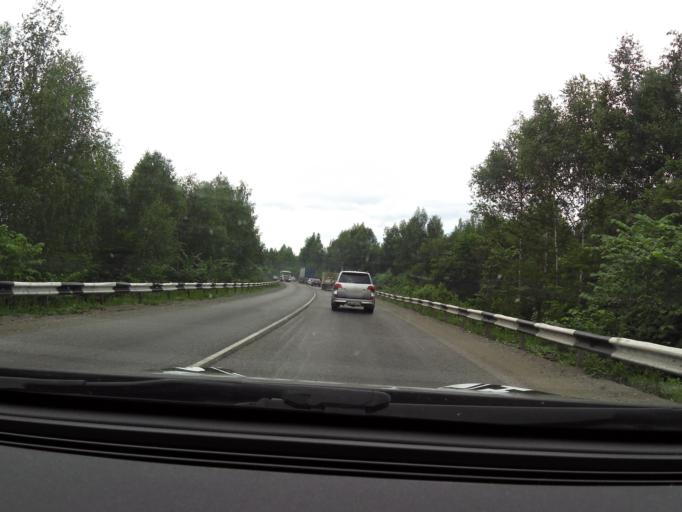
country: RU
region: Chelyabinsk
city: Sim
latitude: 54.9996
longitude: 57.6186
